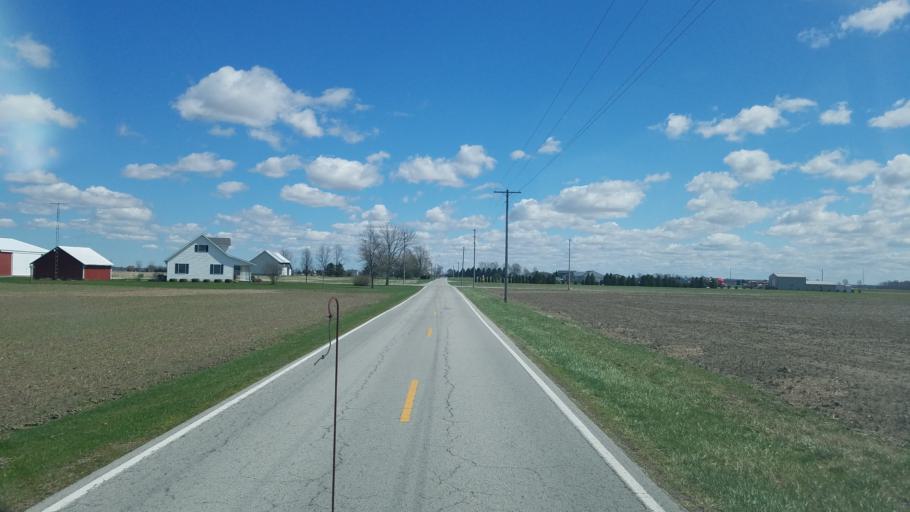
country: US
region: Ohio
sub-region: Hancock County
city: Findlay
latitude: 41.0069
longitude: -83.5372
